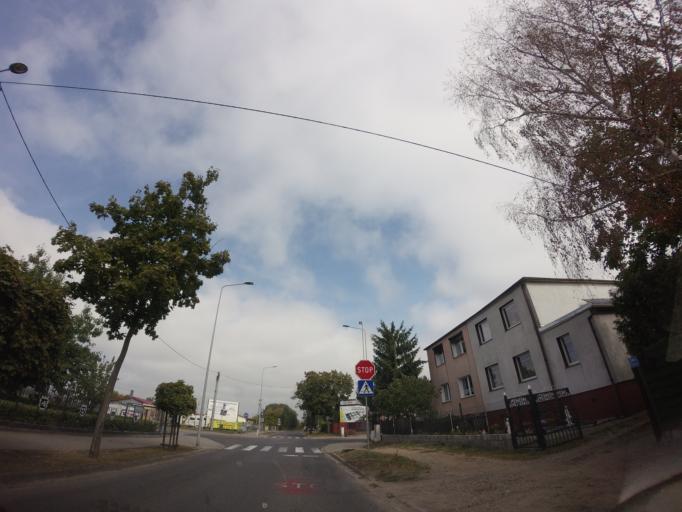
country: PL
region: Greater Poland Voivodeship
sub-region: Powiat miedzychodzki
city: Miedzychod
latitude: 52.6096
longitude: 15.9045
